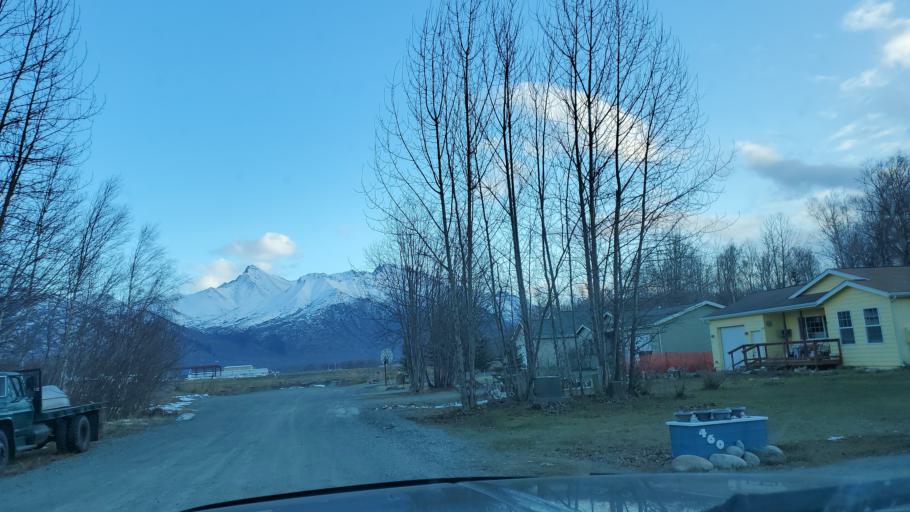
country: US
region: Alaska
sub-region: Matanuska-Susitna Borough
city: Palmer
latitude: 61.5953
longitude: -149.1079
